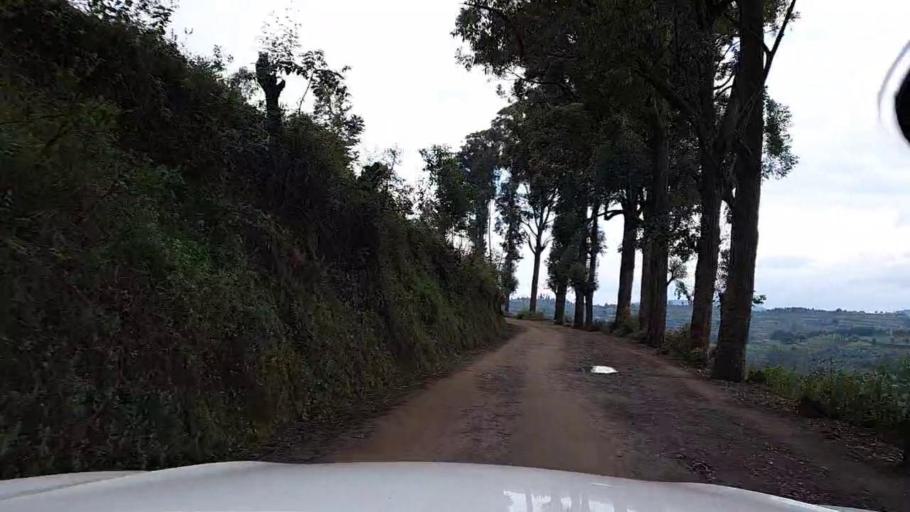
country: BI
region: Kayanza
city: Kayanza
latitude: -2.7944
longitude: 29.5122
